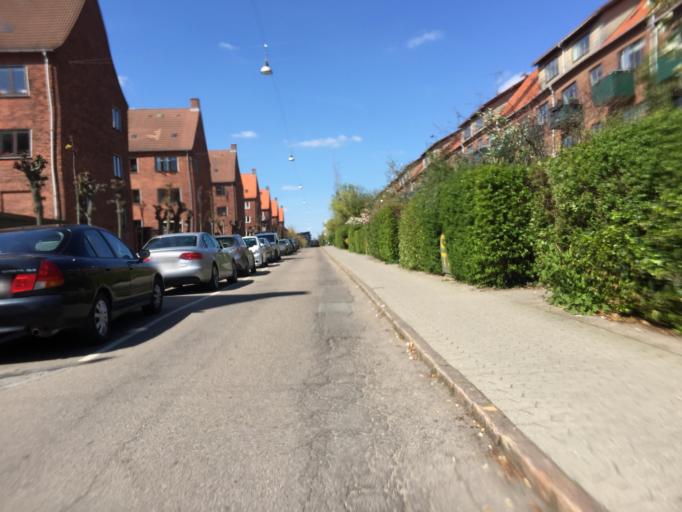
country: DK
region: Capital Region
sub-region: Frederiksberg Kommune
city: Frederiksberg
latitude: 55.6990
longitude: 12.5298
